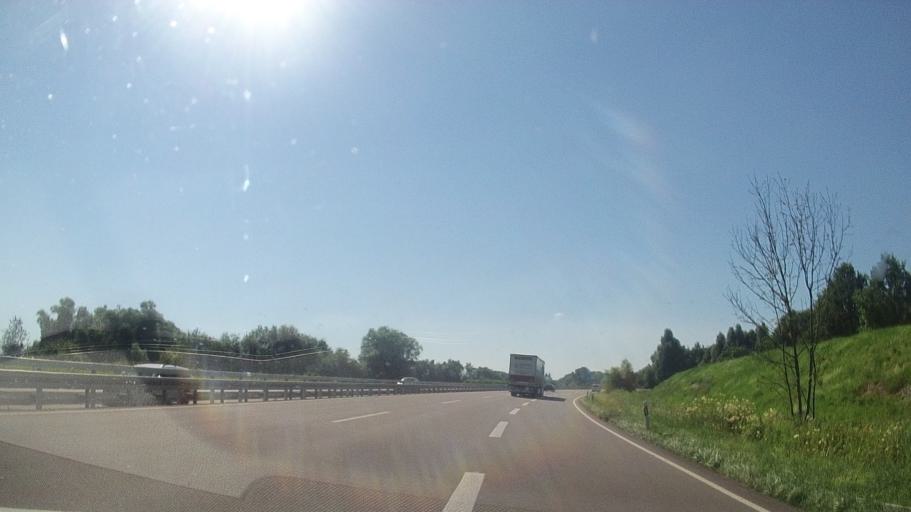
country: DE
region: Baden-Wuerttemberg
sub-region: Freiburg Region
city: Willstatt
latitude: 48.5348
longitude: 7.9188
